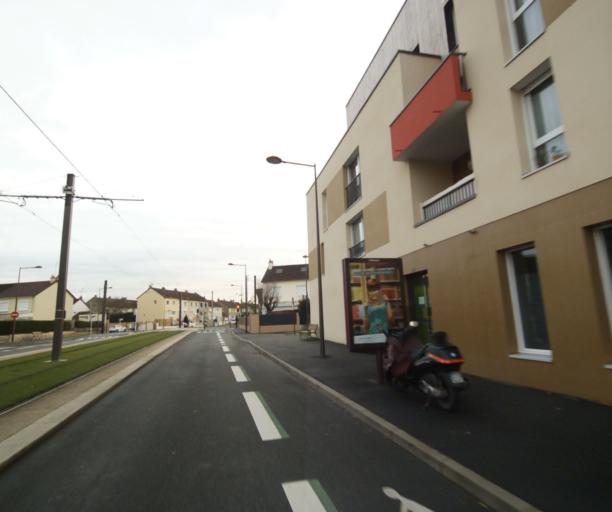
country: FR
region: Pays de la Loire
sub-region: Departement de la Sarthe
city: Coulaines
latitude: 48.0199
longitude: 0.2138
